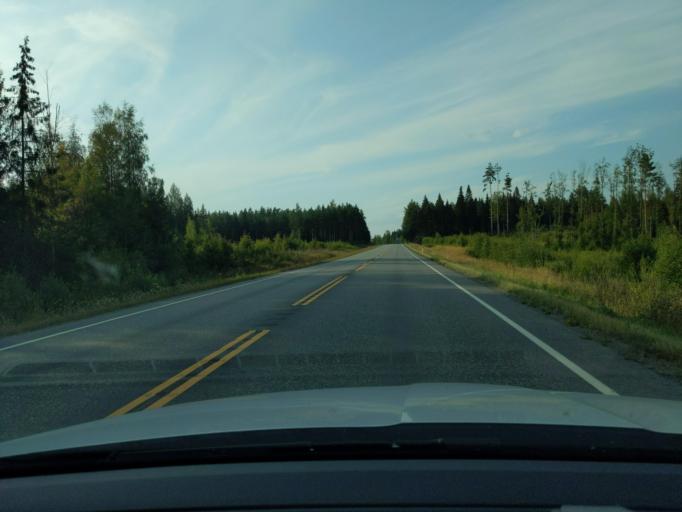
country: FI
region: Paijanne Tavastia
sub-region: Lahti
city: Padasjoki
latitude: 61.3300
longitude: 25.2714
